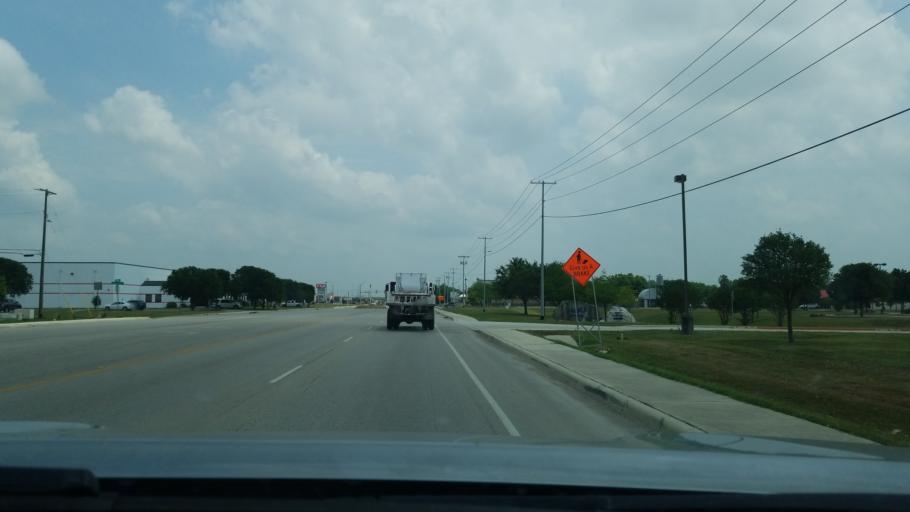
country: US
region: Texas
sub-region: Comal County
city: New Braunfels
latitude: 29.7340
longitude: -98.0843
